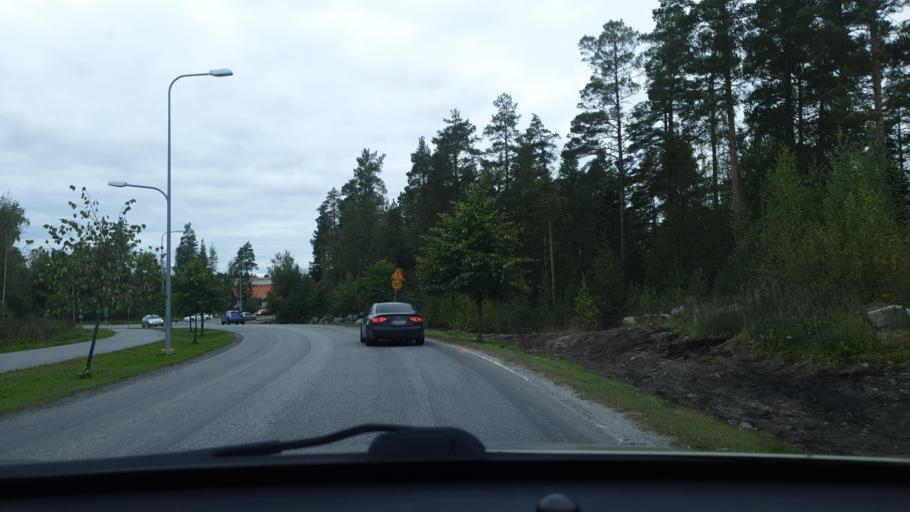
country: FI
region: Ostrobothnia
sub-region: Vaasa
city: Korsholm
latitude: 63.1187
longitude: 21.6585
